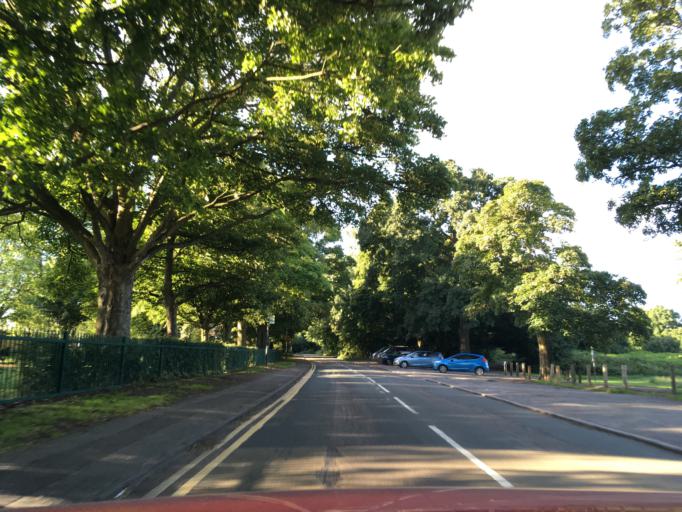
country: GB
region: England
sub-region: South Gloucestershire
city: Mangotsfield
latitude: 51.4797
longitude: -2.4847
